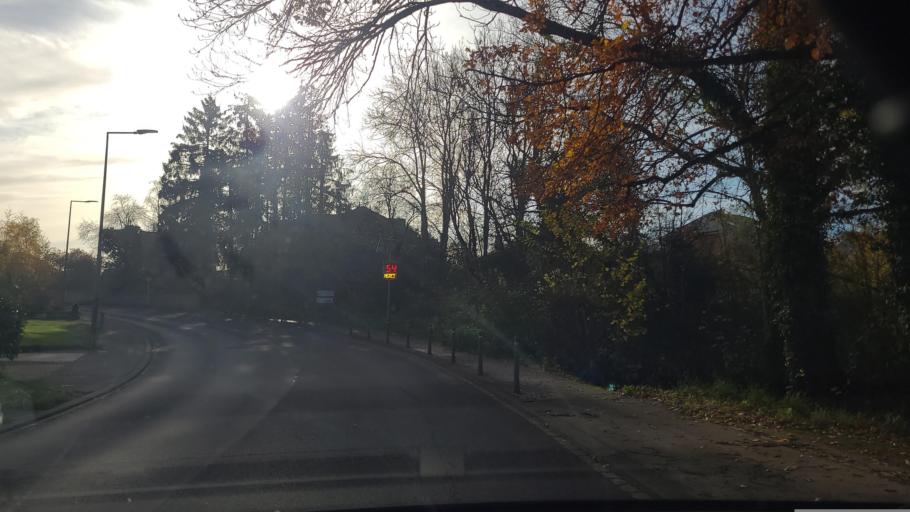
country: LU
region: Luxembourg
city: Hautcharage
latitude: 49.5820
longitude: 5.9088
